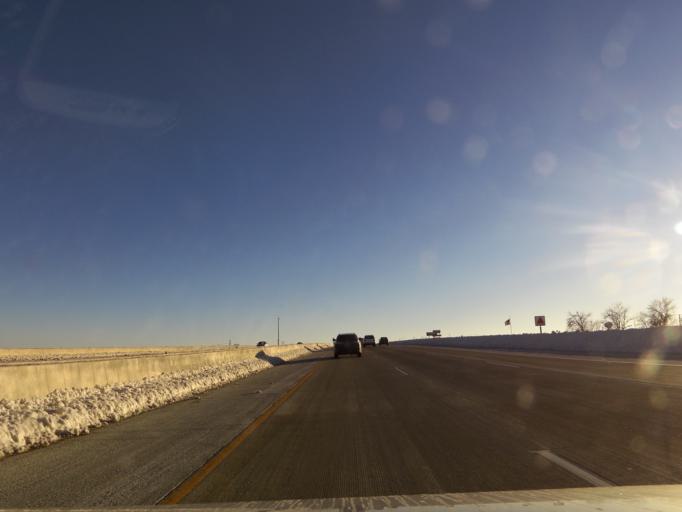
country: US
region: Wisconsin
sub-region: Racine County
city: Franksville
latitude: 42.7283
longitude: -87.9541
